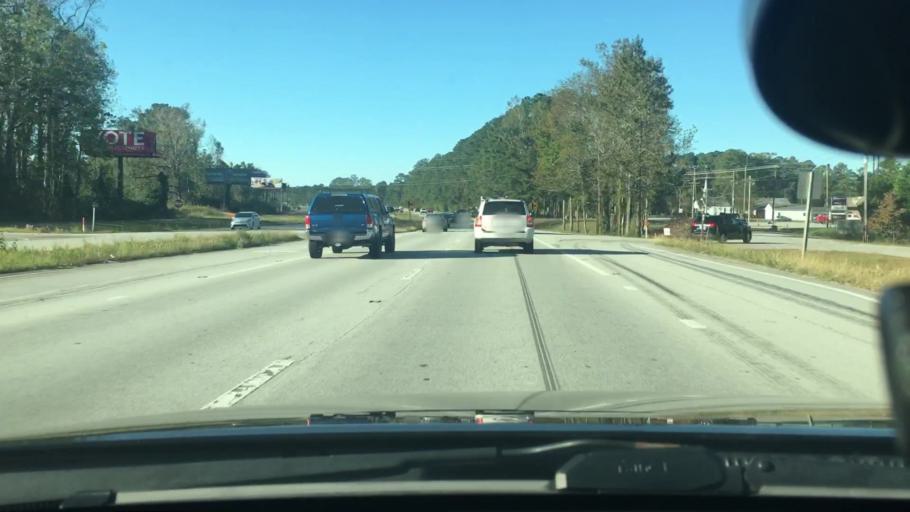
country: US
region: North Carolina
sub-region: Craven County
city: Neuse Forest
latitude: 34.9534
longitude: -76.9490
